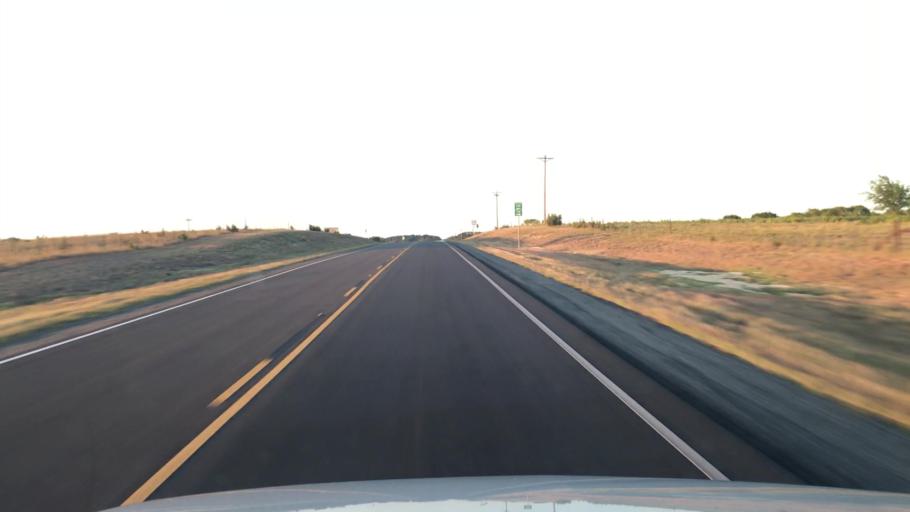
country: US
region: Texas
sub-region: Hamilton County
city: Hico
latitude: 32.0807
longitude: -97.9795
